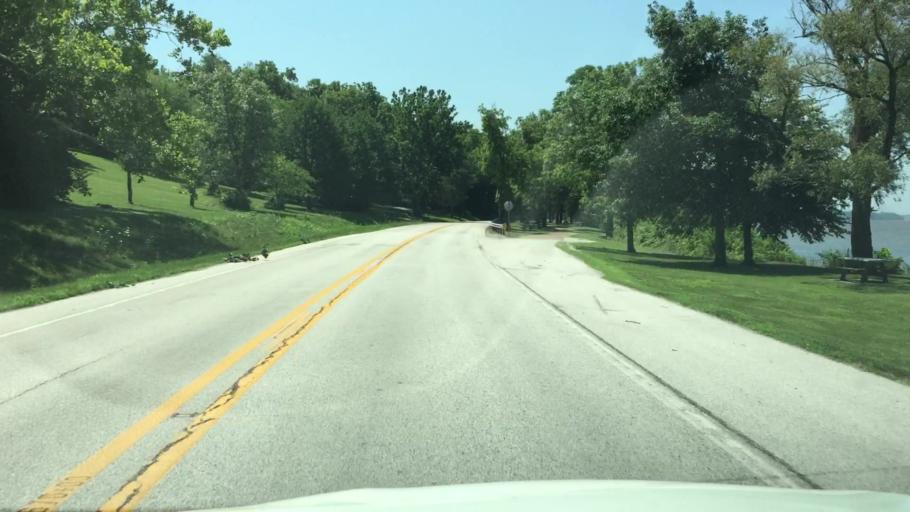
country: US
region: Illinois
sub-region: Hancock County
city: Nauvoo
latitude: 40.5094
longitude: -91.3577
